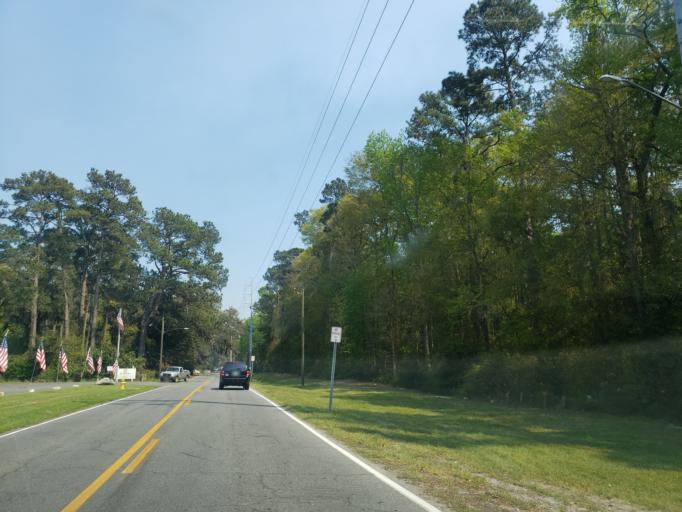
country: US
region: Georgia
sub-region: Chatham County
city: Isle of Hope
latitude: 32.0125
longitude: -81.0775
